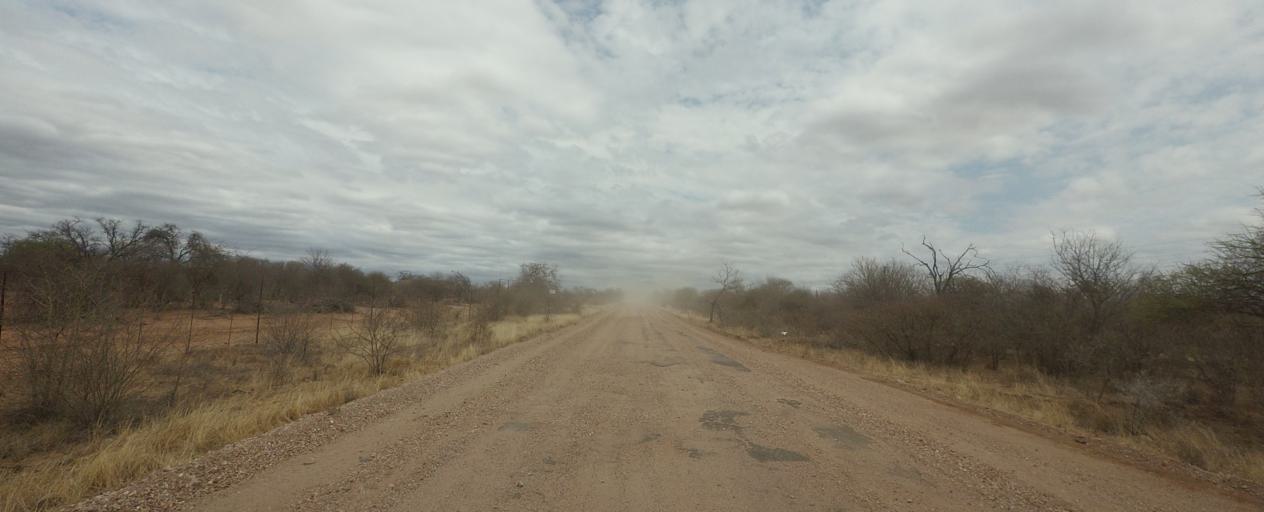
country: BW
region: Central
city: Mathathane
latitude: -22.6761
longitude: 28.6707
